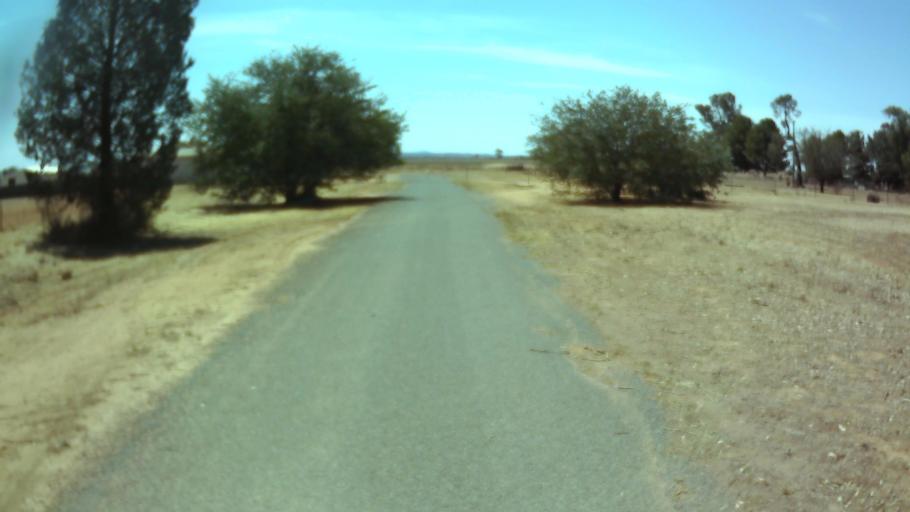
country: AU
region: New South Wales
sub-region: Weddin
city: Grenfell
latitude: -33.8406
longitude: 147.7396
